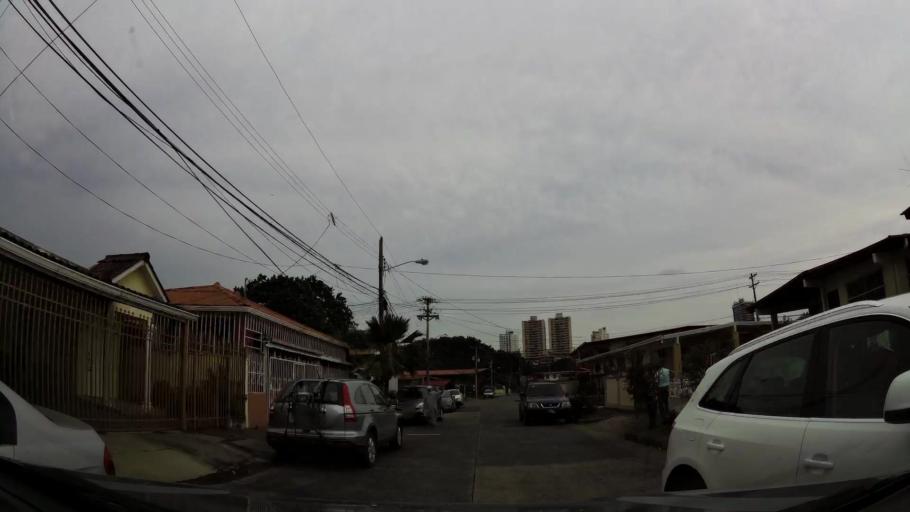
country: PA
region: Panama
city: Panama
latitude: 9.0214
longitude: -79.5227
